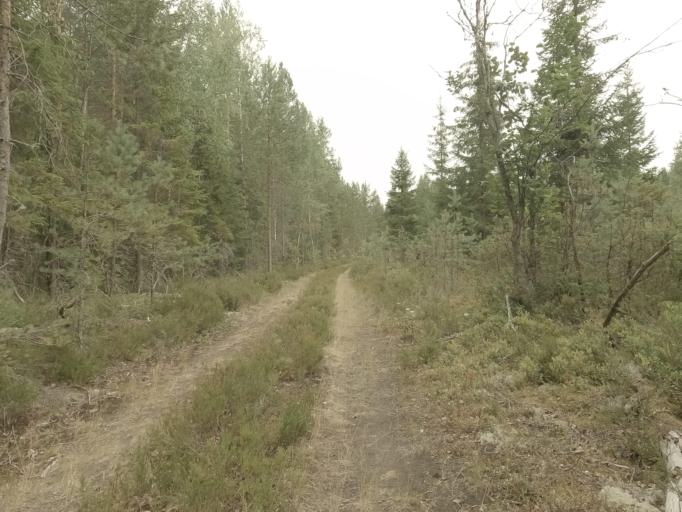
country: RU
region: Leningrad
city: Kamennogorsk
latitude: 61.0441
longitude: 29.1866
